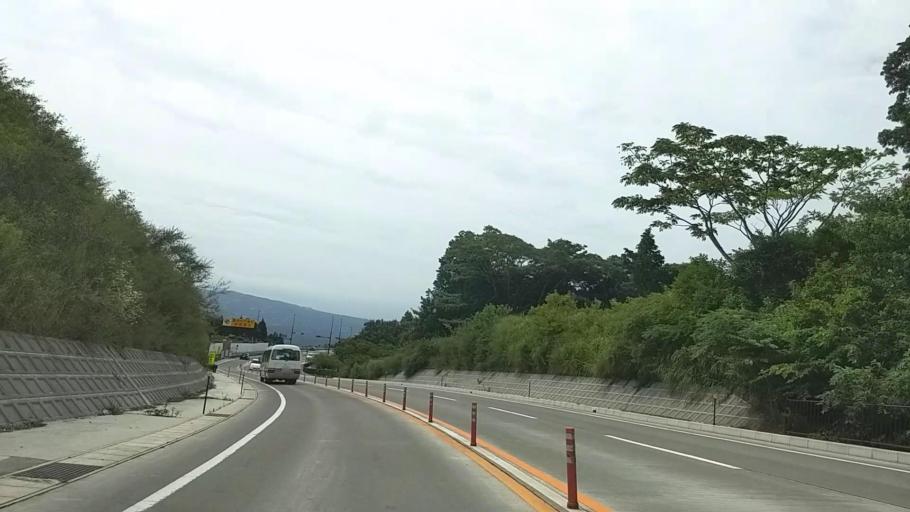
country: JP
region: Kanagawa
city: Hakone
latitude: 35.1531
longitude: 138.9900
